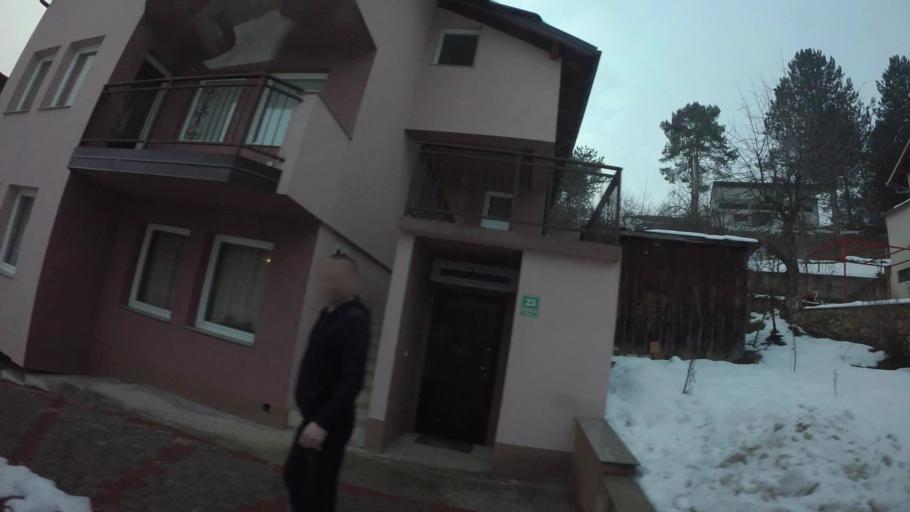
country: BA
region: Federation of Bosnia and Herzegovina
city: Vogosca
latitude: 43.9056
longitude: 18.3491
